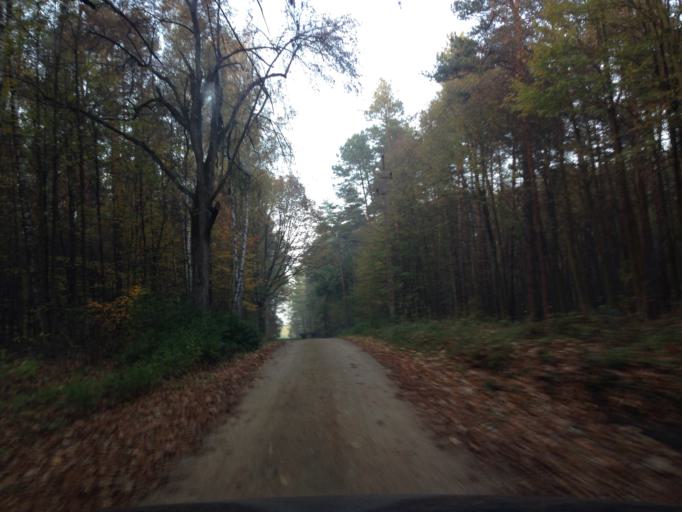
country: PL
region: Warmian-Masurian Voivodeship
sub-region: Powiat dzialdowski
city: Lidzbark
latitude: 53.2514
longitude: 19.7649
